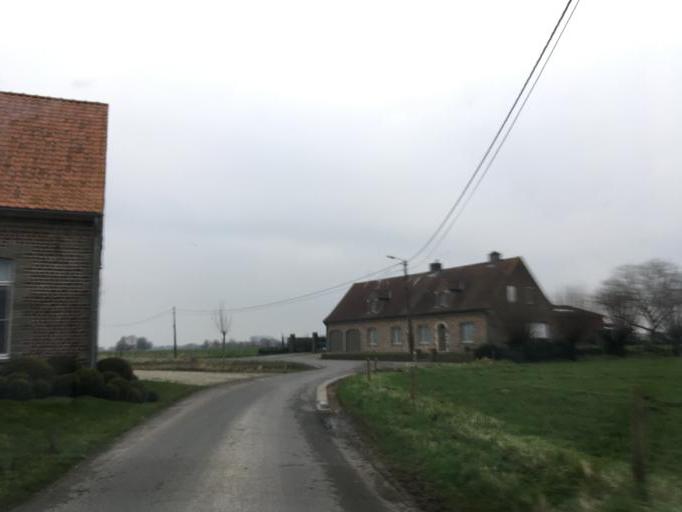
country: BE
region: Flanders
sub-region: Provincie West-Vlaanderen
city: Hooglede
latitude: 50.9717
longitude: 3.0969
